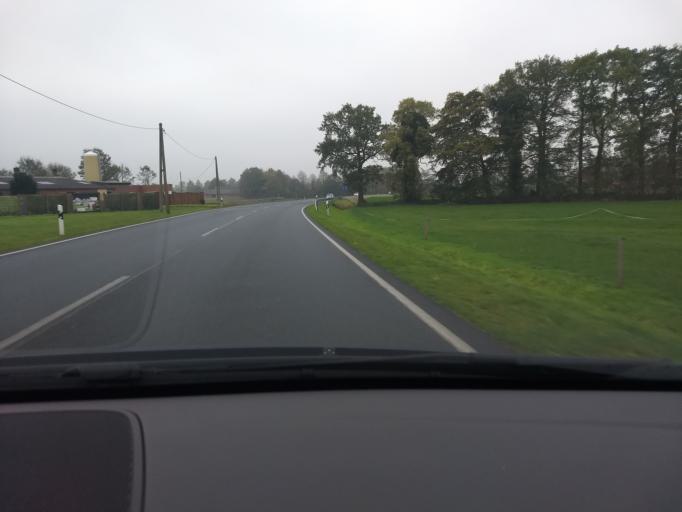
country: DE
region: North Rhine-Westphalia
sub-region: Regierungsbezirk Munster
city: Sudlohn
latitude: 51.9246
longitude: 6.8464
